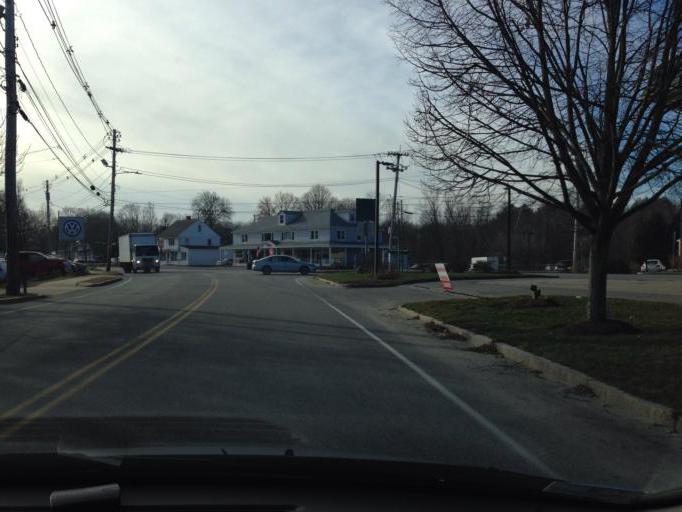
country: US
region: Massachusetts
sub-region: Middlesex County
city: Bedford
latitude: 42.4962
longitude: -71.2855
